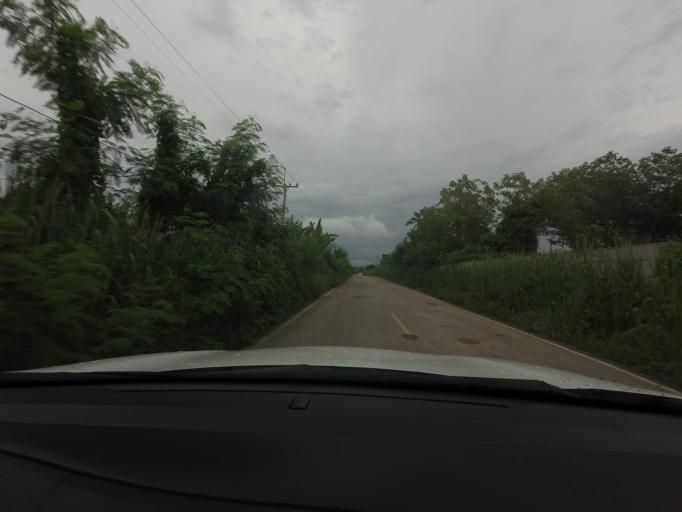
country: TH
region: Nakhon Ratchasima
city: Pak Chong
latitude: 14.6590
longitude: 101.4220
